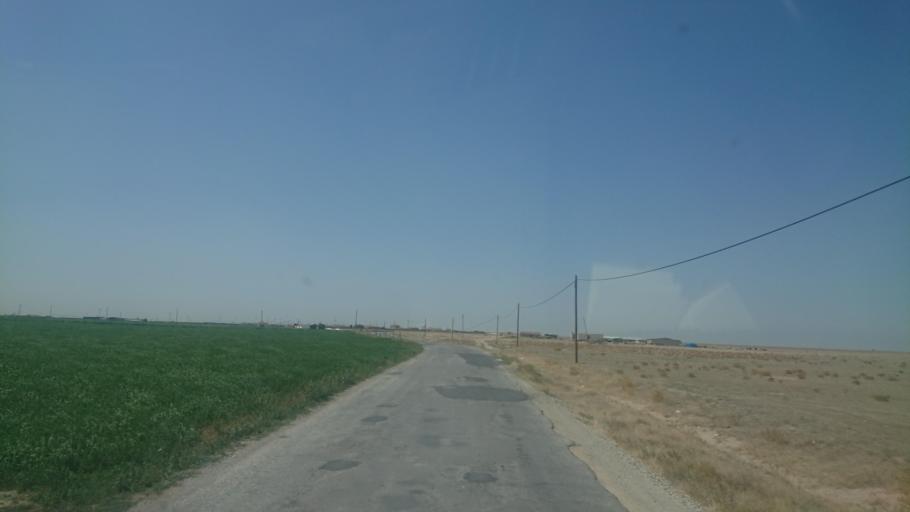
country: TR
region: Aksaray
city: Yesilova
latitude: 38.2952
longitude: 33.7267
